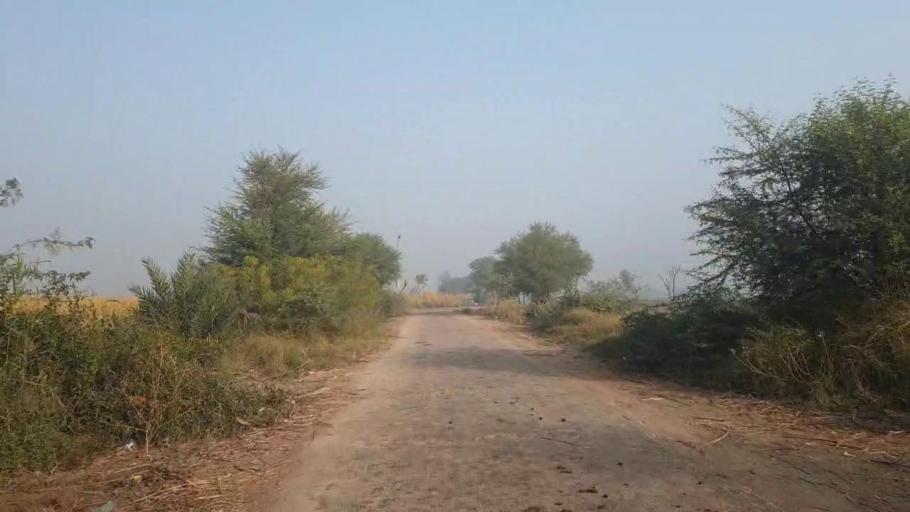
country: PK
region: Sindh
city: Tando Adam
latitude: 25.8165
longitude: 68.6323
